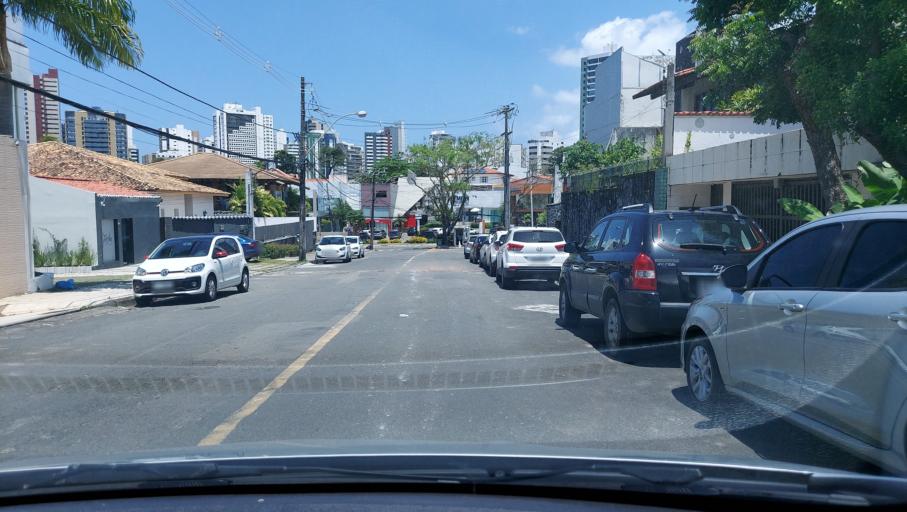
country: BR
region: Bahia
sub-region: Salvador
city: Salvador
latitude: -12.9824
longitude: -38.4579
